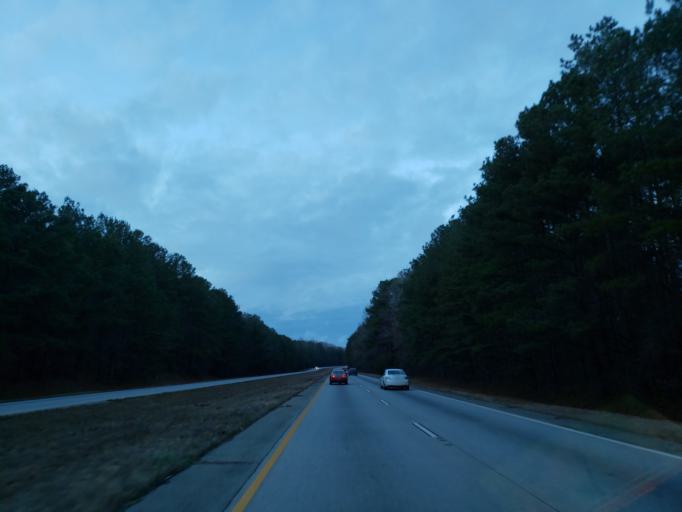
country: US
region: Georgia
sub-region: Fulton County
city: Union City
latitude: 33.6896
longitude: -84.5739
